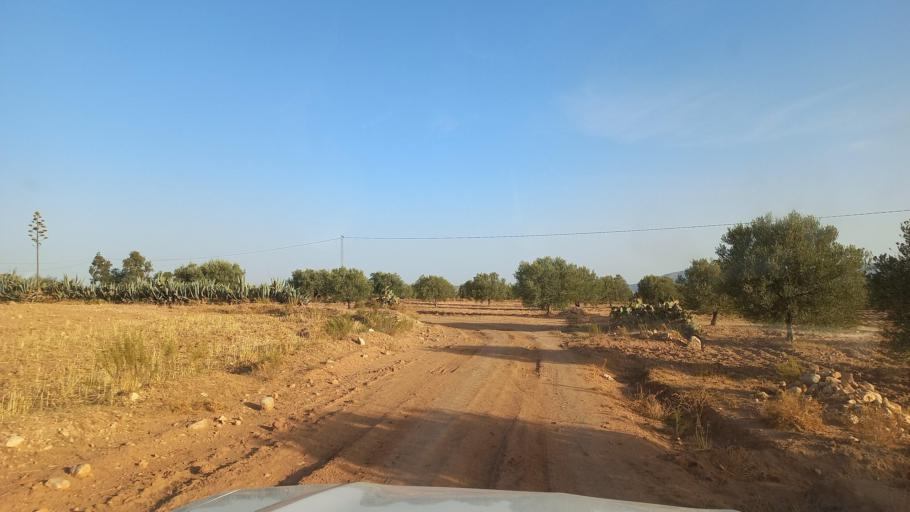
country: TN
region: Al Qasrayn
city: Kasserine
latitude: 35.2568
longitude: 8.9077
